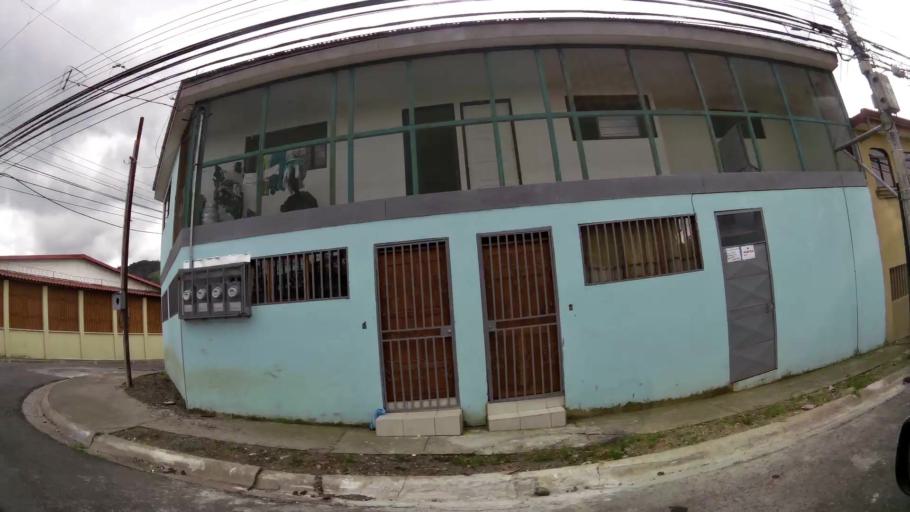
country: CR
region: San Jose
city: San Felipe
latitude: 9.9151
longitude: -84.1174
